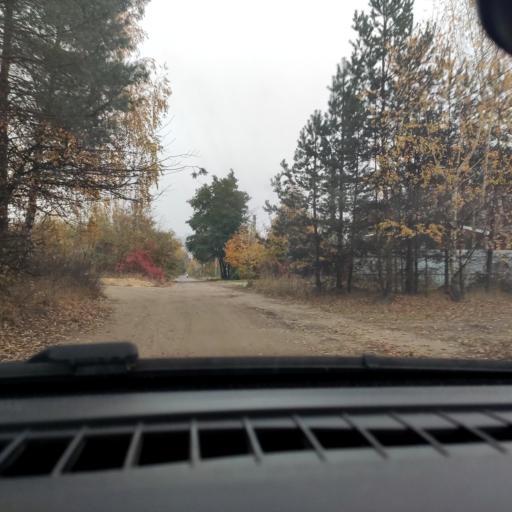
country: RU
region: Voronezj
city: Podgornoye
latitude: 51.7674
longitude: 39.1829
